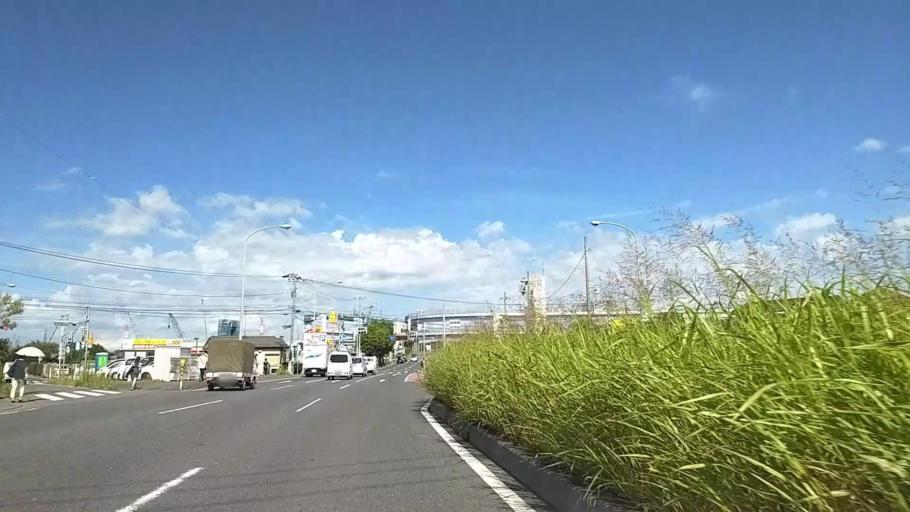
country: JP
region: Kanagawa
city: Yokohama
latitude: 35.5139
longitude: 139.5973
